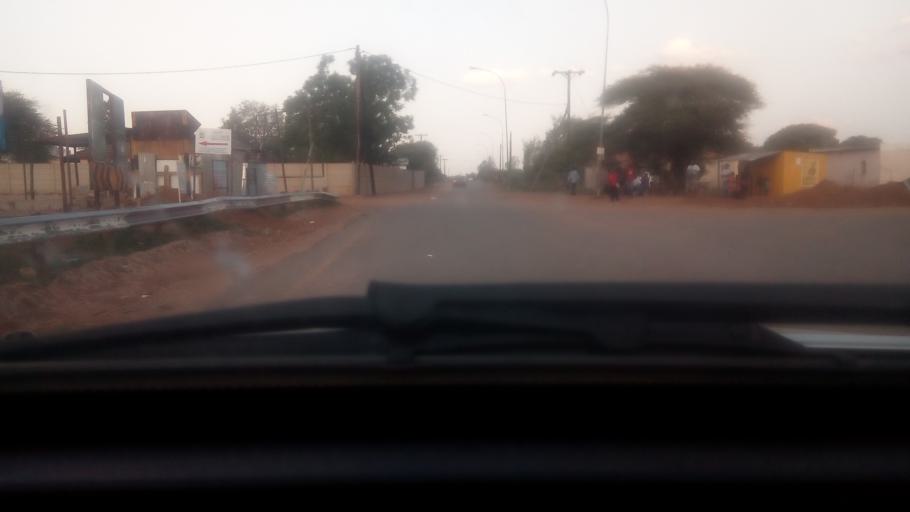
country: BW
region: Kgatleng
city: Bokaa
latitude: -24.4265
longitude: 26.0170
